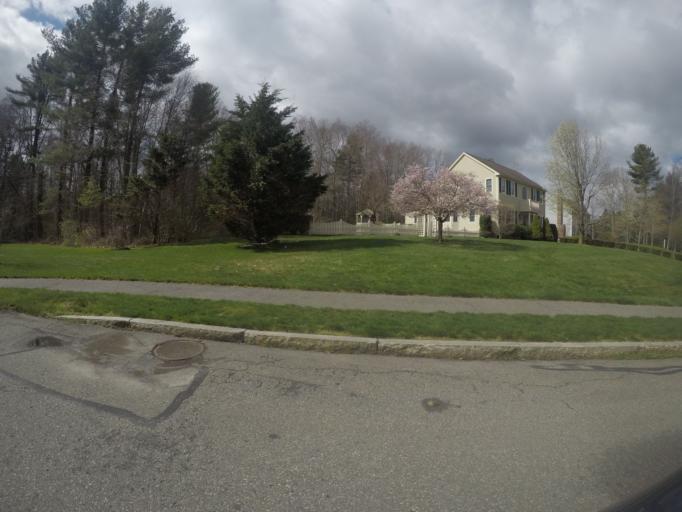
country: US
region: Massachusetts
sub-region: Bristol County
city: Easton
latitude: 42.0333
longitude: -71.1185
